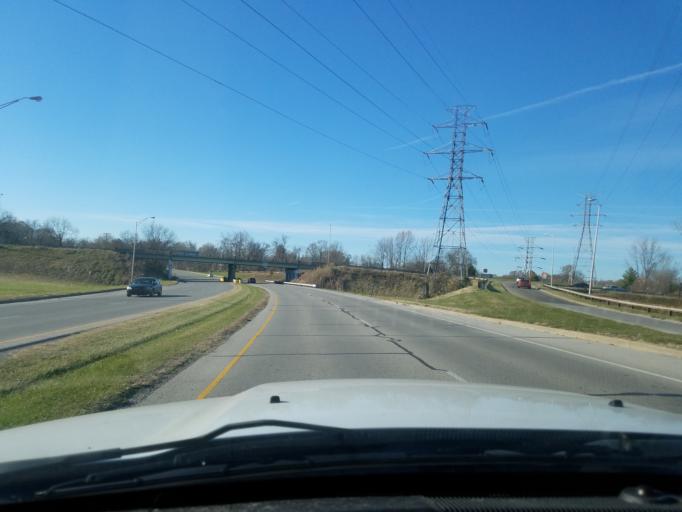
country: US
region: Indiana
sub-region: Clark County
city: Clarksville
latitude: 38.3024
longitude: -85.7801
